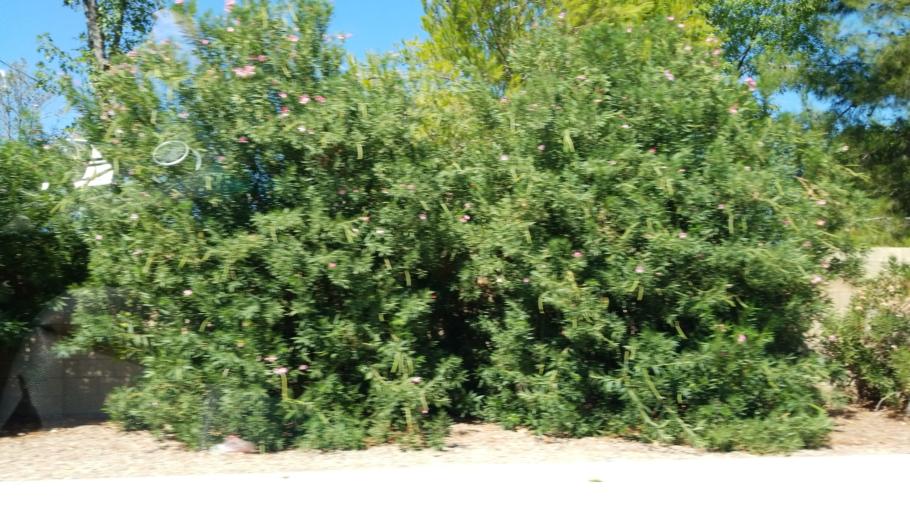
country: US
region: Arizona
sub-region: Maricopa County
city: Peoria
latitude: 33.6059
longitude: -112.2028
